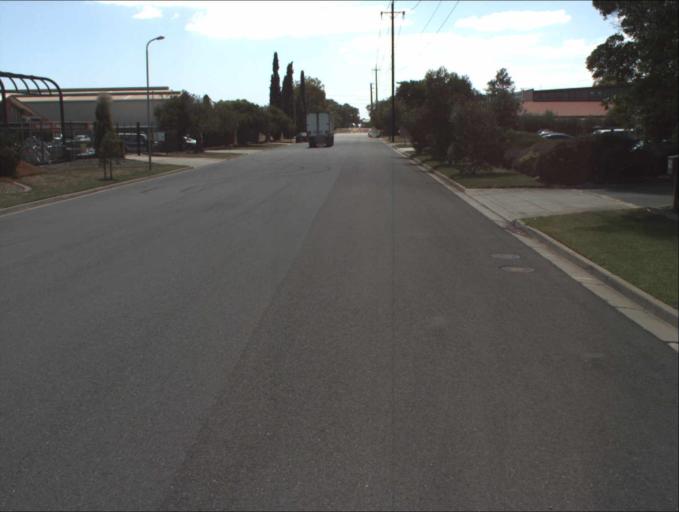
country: AU
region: South Australia
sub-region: Port Adelaide Enfield
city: Blair Athol
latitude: -34.8531
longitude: 138.5698
